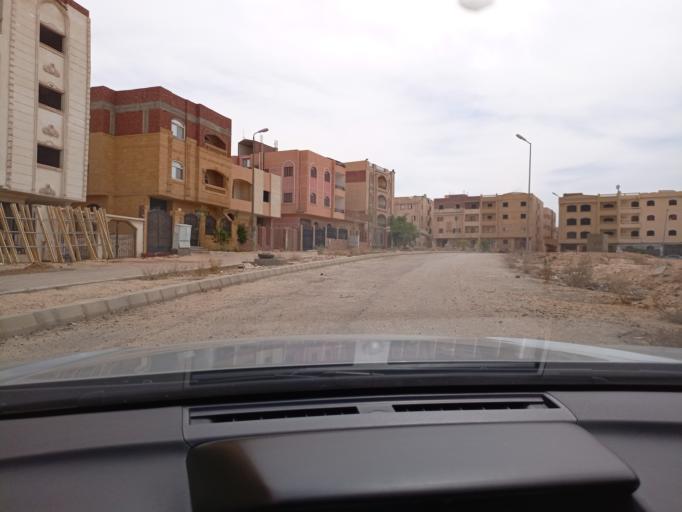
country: EG
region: Muhafazat al Qalyubiyah
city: Al Khankah
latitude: 30.2443
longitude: 31.4956
